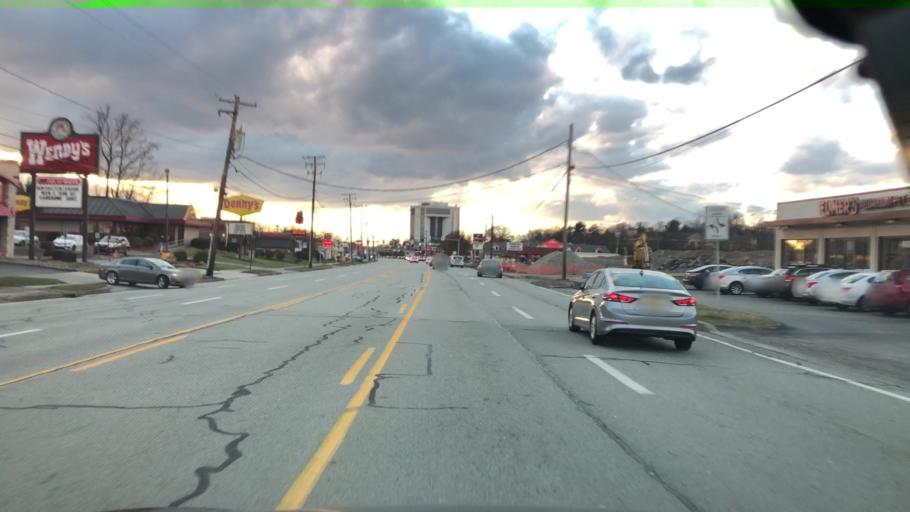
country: US
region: Pennsylvania
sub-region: Allegheny County
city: Monroeville
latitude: 40.4386
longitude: -79.7713
